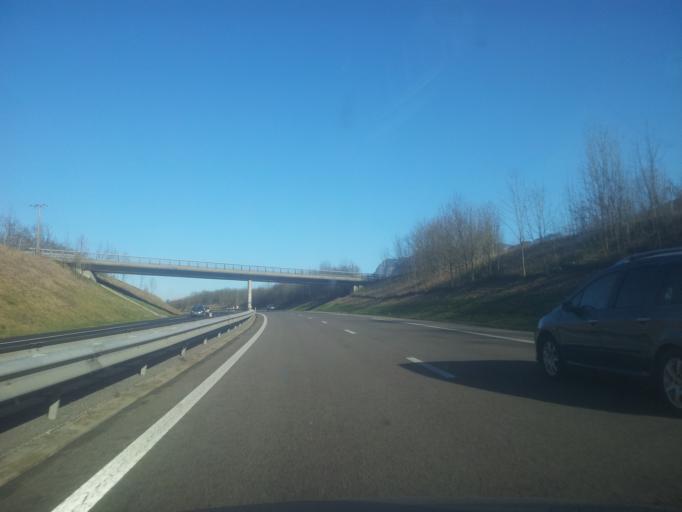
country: FR
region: Rhone-Alpes
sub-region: Departement de l'Isere
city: Vinay
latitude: 45.1783
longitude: 5.3981
